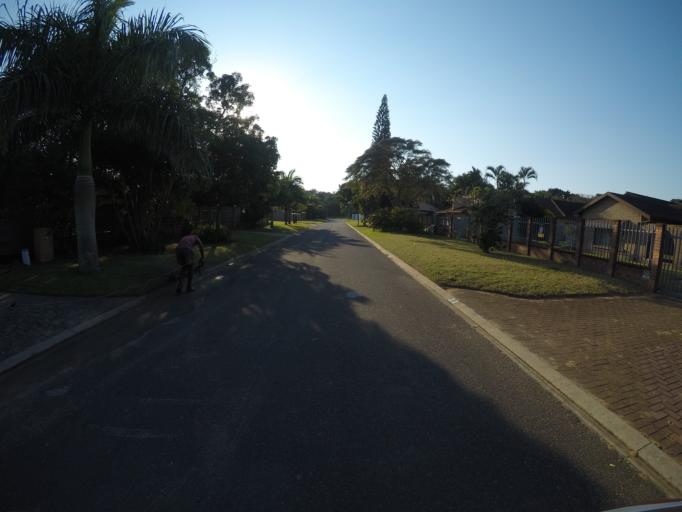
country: ZA
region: KwaZulu-Natal
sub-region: uThungulu District Municipality
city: Richards Bay
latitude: -28.7803
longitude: 32.1129
